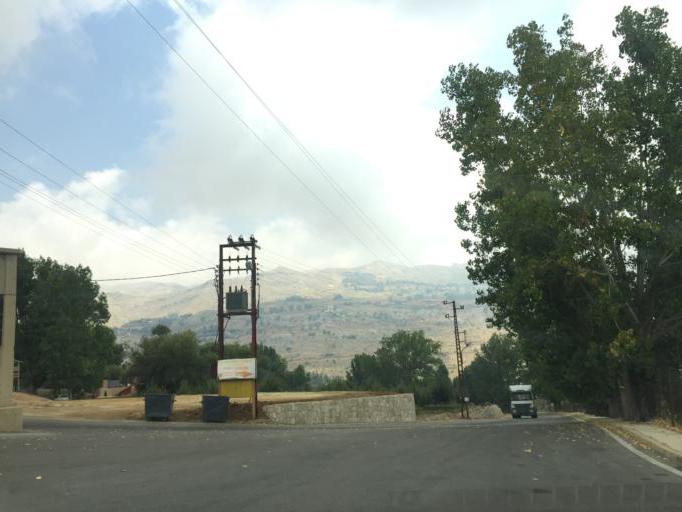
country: LB
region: Beqaa
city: Zahle
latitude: 34.0009
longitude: 35.8062
